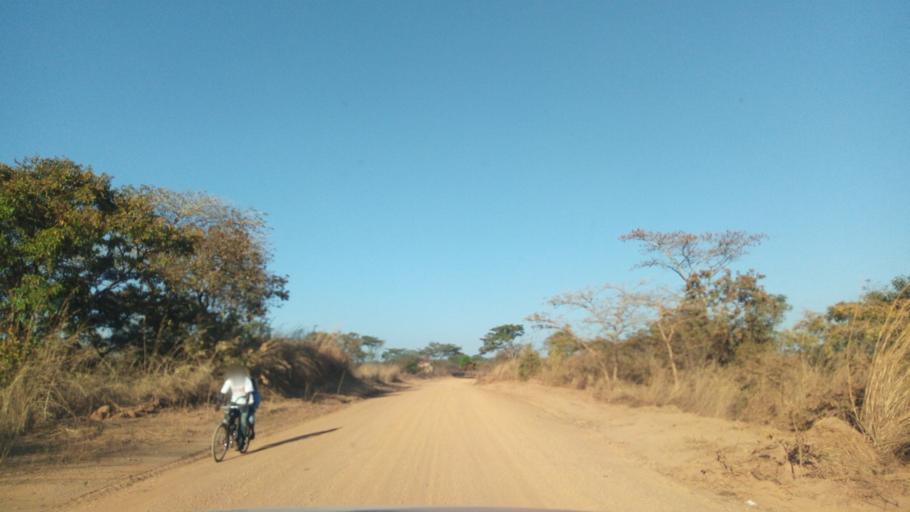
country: ZM
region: Luapula
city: Mwense
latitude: -10.4501
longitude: 28.5558
